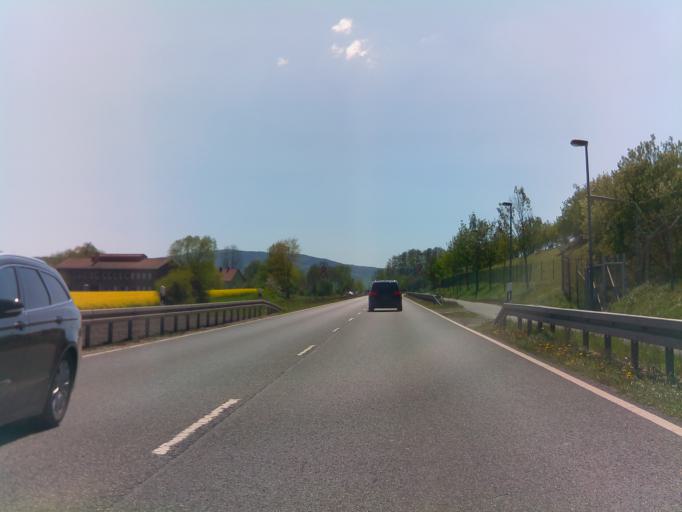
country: DE
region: Hesse
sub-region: Regierungsbezirk Kassel
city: Bad Hersfeld
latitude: 50.8490
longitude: 9.6833
